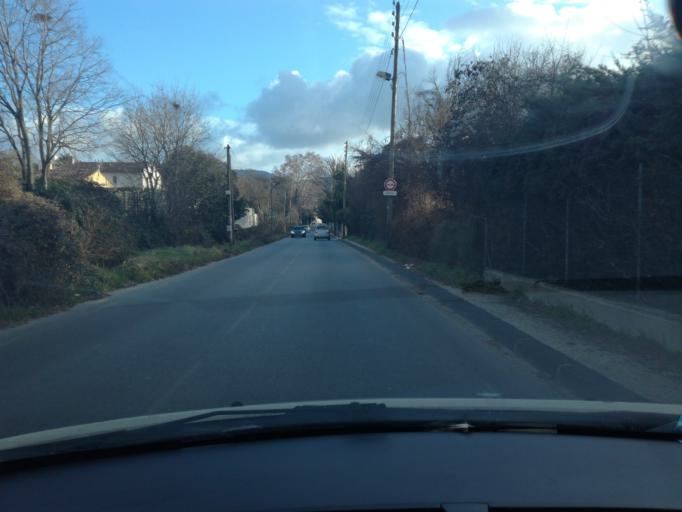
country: FR
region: Provence-Alpes-Cote d'Azur
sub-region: Departement des Bouches-du-Rhone
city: La Penne-sur-Huveaune
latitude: 43.3034
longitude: 5.5007
